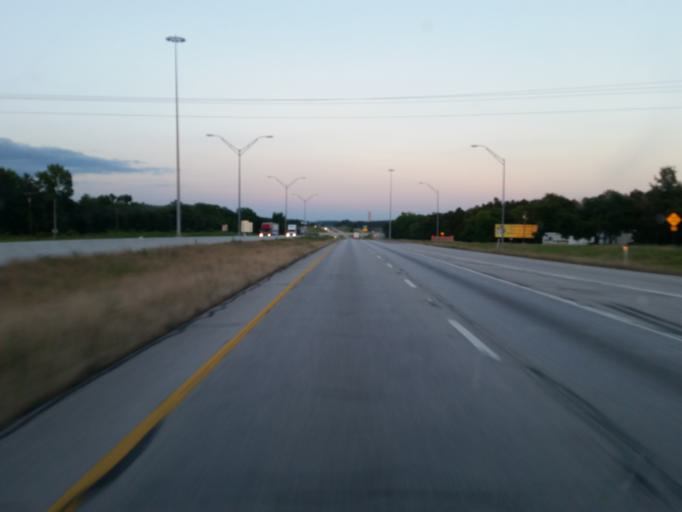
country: US
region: Texas
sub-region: Smith County
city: Hideaway
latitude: 32.4696
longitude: -95.4495
